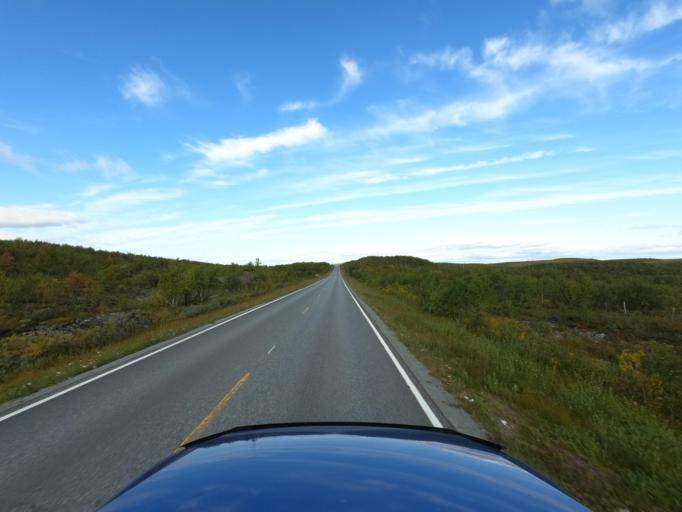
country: NO
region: Finnmark Fylke
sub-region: Karasjok
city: Karasjohka
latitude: 69.6903
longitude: 25.2597
